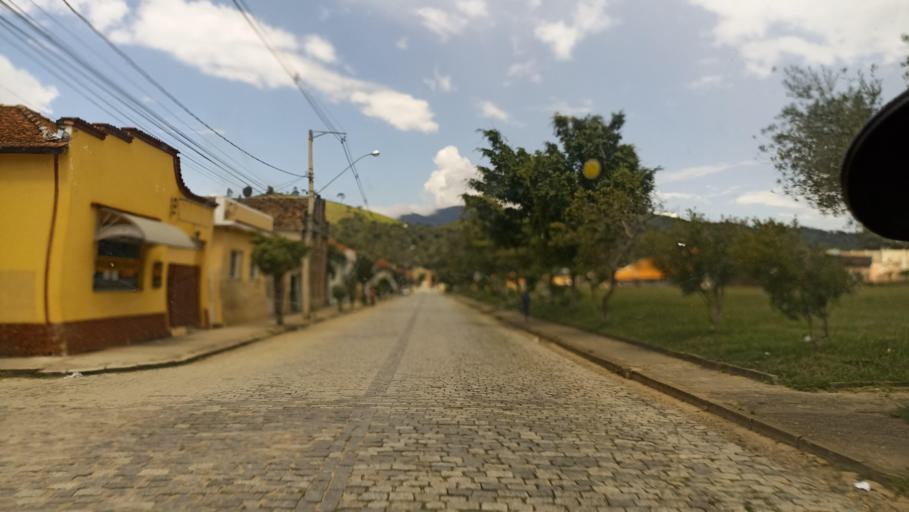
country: BR
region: Minas Gerais
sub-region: Passa Quatro
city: Passa Quatro
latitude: -22.3885
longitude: -44.9653
